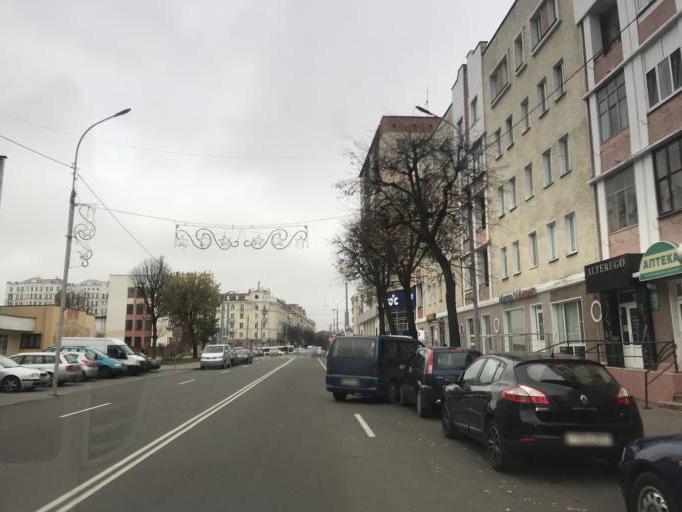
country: BY
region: Mogilev
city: Mahilyow
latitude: 53.8965
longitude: 30.3318
